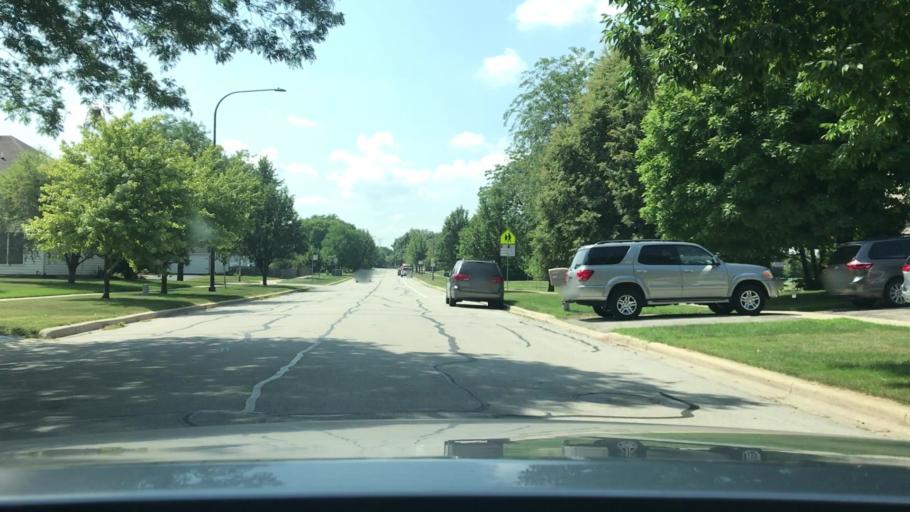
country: US
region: Illinois
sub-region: DuPage County
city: Woodridge
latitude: 41.7420
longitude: -88.0960
